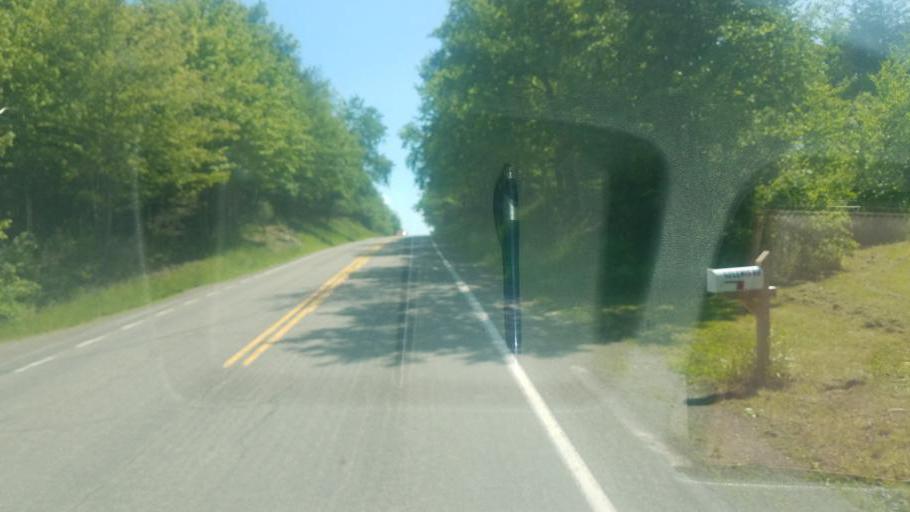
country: US
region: Pennsylvania
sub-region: Tioga County
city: Wellsboro
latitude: 41.7317
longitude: -77.3802
